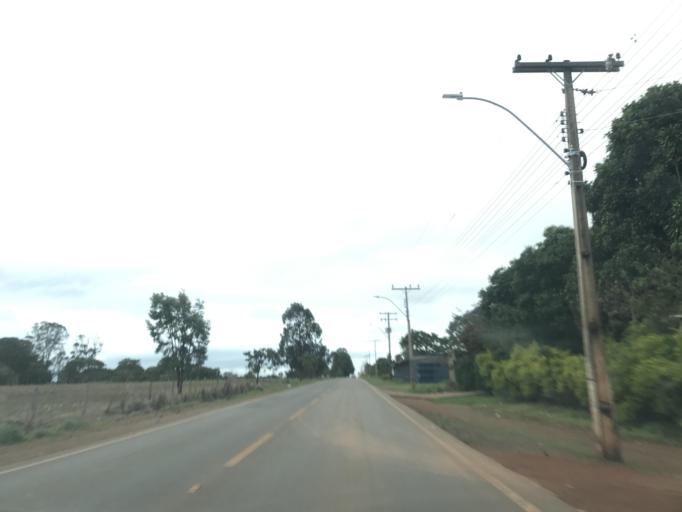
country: BR
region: Goias
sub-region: Luziania
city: Luziania
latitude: -16.3185
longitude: -48.0171
